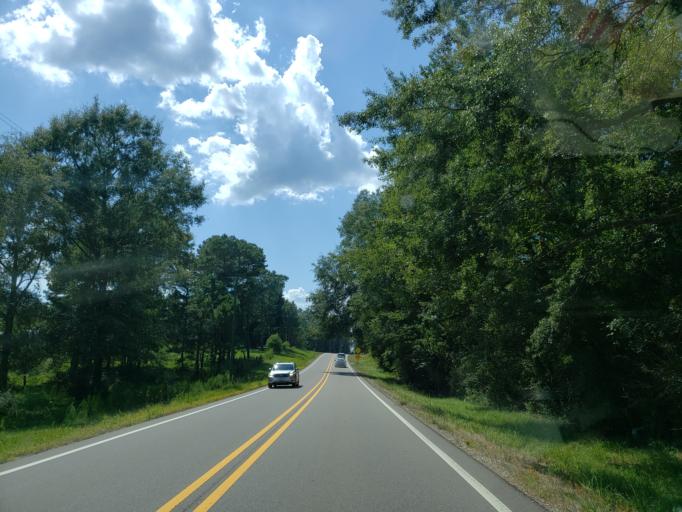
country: US
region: Mississippi
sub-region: Lamar County
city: Sumrall
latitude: 31.3867
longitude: -89.5315
